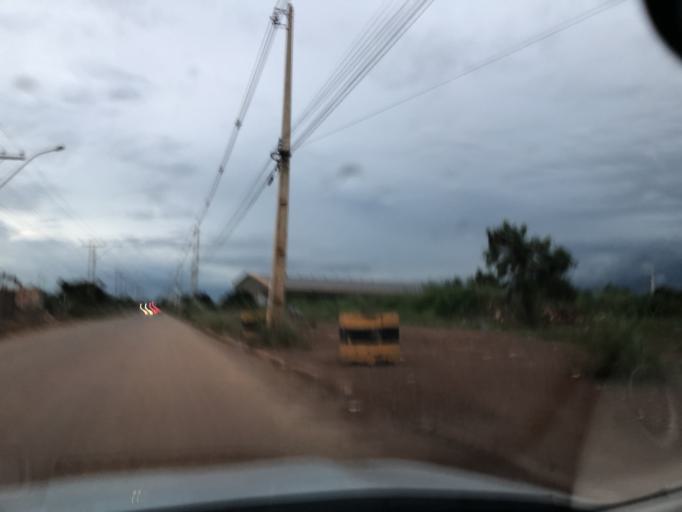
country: BR
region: Goias
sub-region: Luziania
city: Luziania
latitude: -16.1083
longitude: -47.9799
